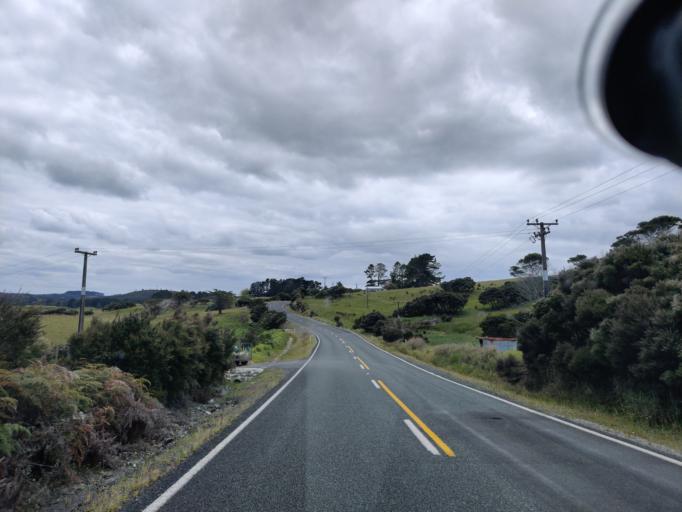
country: NZ
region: Northland
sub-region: Far North District
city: Kaitaia
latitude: -34.6426
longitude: 172.9700
